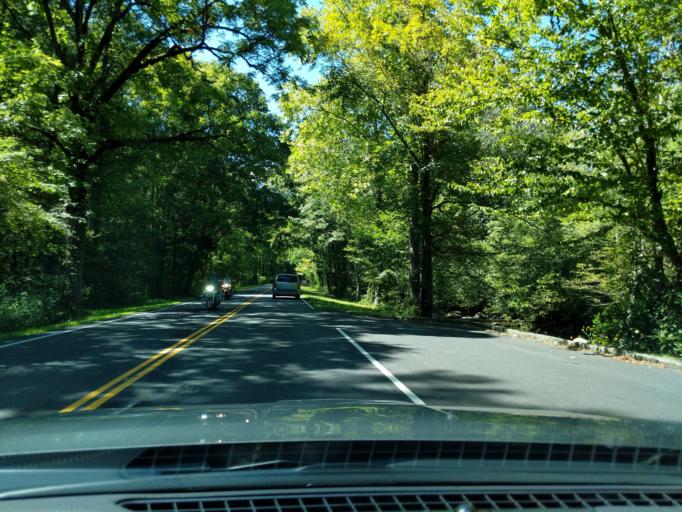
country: US
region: North Carolina
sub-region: Swain County
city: Cherokee
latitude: 35.5570
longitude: -83.3194
